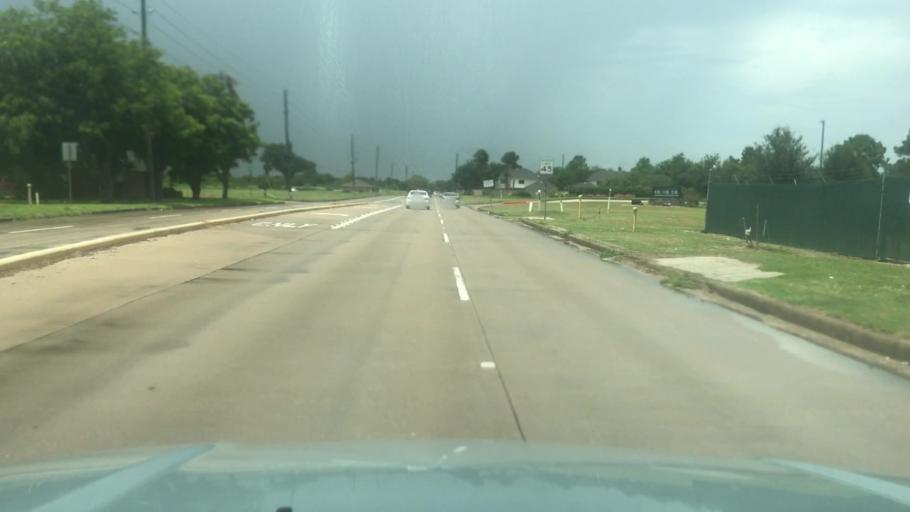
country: US
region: Texas
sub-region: Harris County
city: Katy
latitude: 29.7586
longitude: -95.8083
